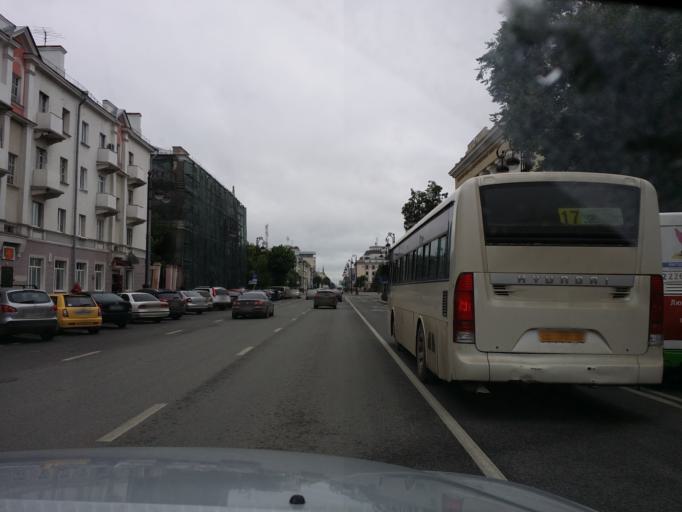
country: RU
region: Tjumen
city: Tyumen
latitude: 57.1515
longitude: 65.5437
